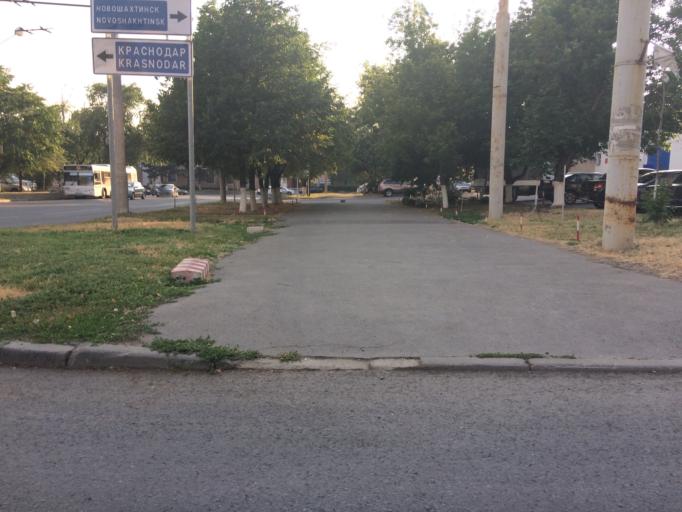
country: RU
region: Rostov
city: Rostov-na-Donu
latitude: 47.2077
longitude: 39.6149
